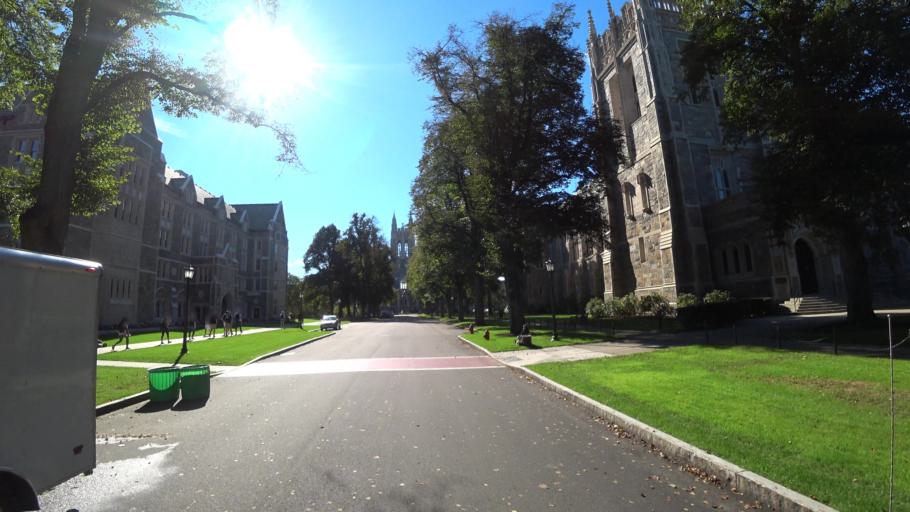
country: US
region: Massachusetts
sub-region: Middlesex County
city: Watertown
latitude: 42.3372
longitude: -71.1712
